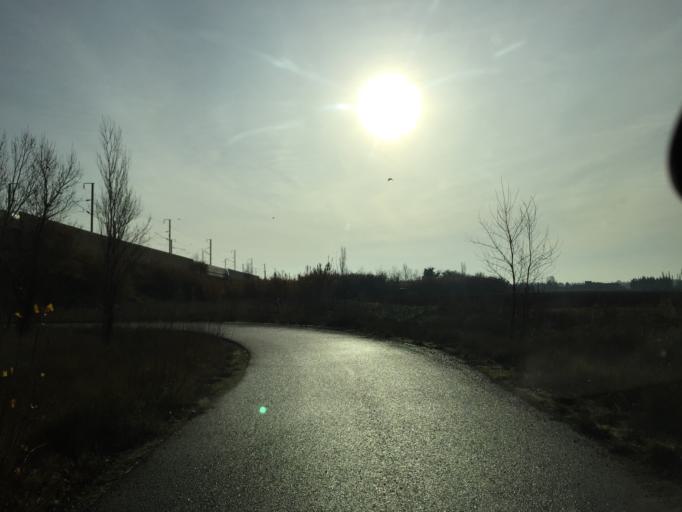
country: FR
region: Provence-Alpes-Cote d'Azur
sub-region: Departement du Vaucluse
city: Piolenc
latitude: 44.1442
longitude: 4.7574
